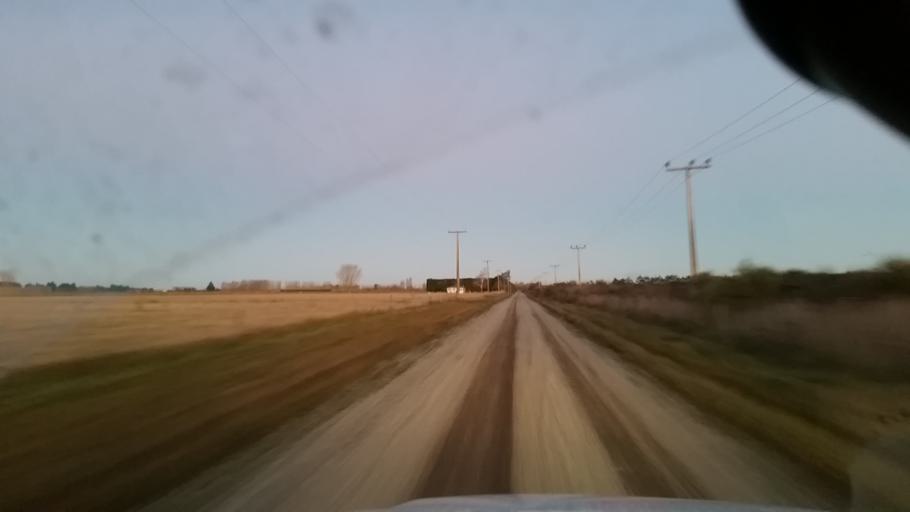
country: NZ
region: Canterbury
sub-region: Ashburton District
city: Tinwald
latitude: -43.9943
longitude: 171.6607
